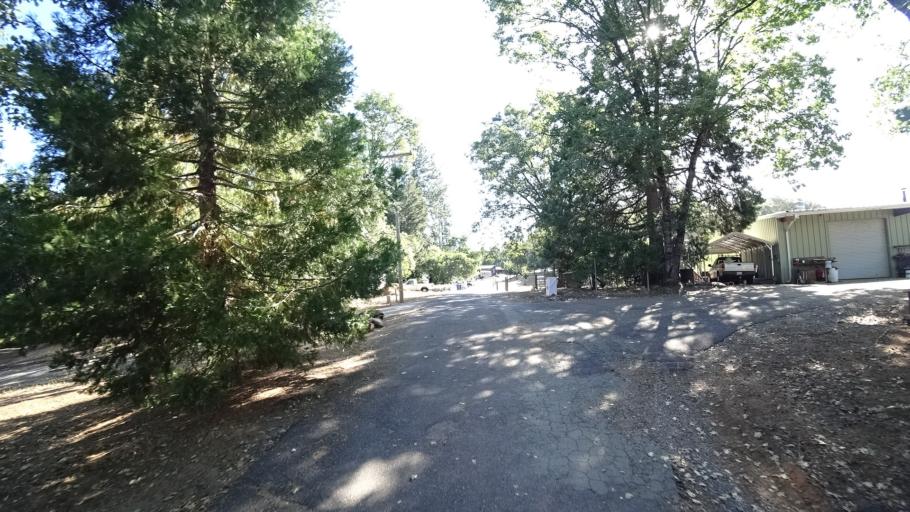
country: US
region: California
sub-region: Amador County
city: Pioneer
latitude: 38.4118
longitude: -120.5549
